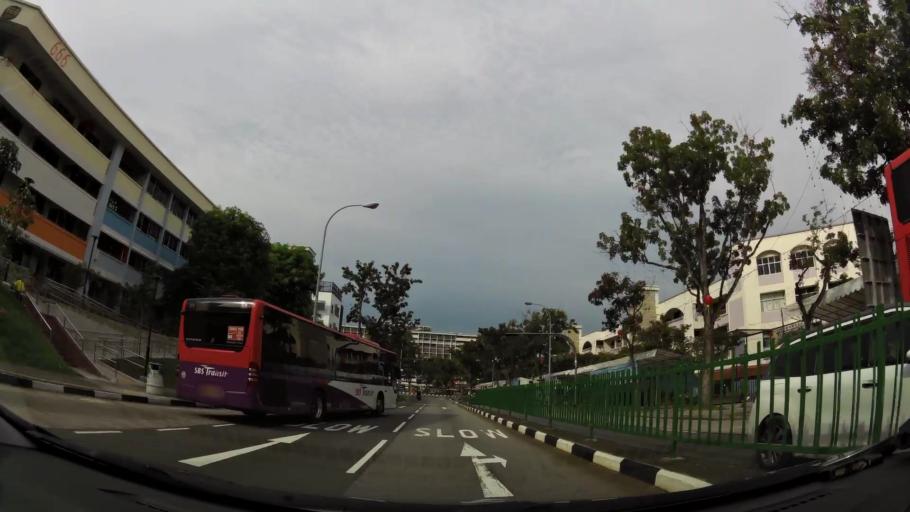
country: SG
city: Singapore
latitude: 1.3735
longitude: 103.8851
